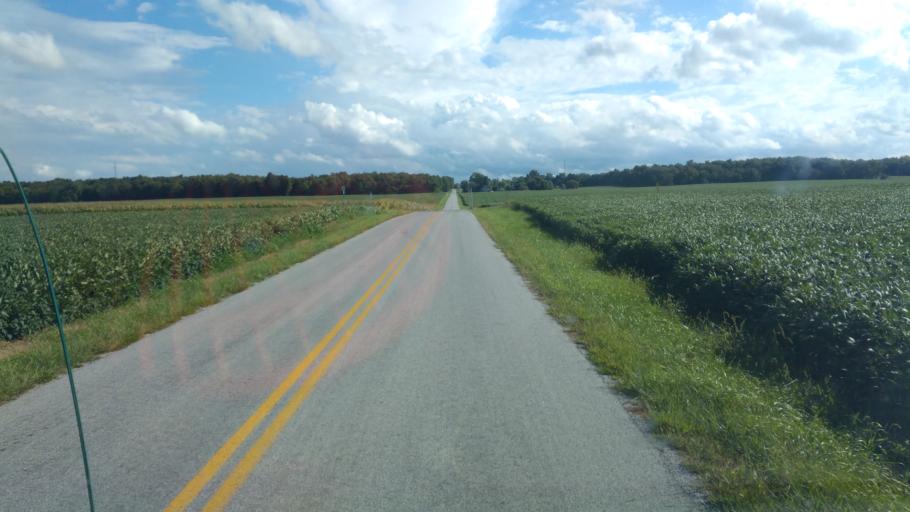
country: US
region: Ohio
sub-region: Hardin County
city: Kenton
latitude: 40.6760
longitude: -83.6336
